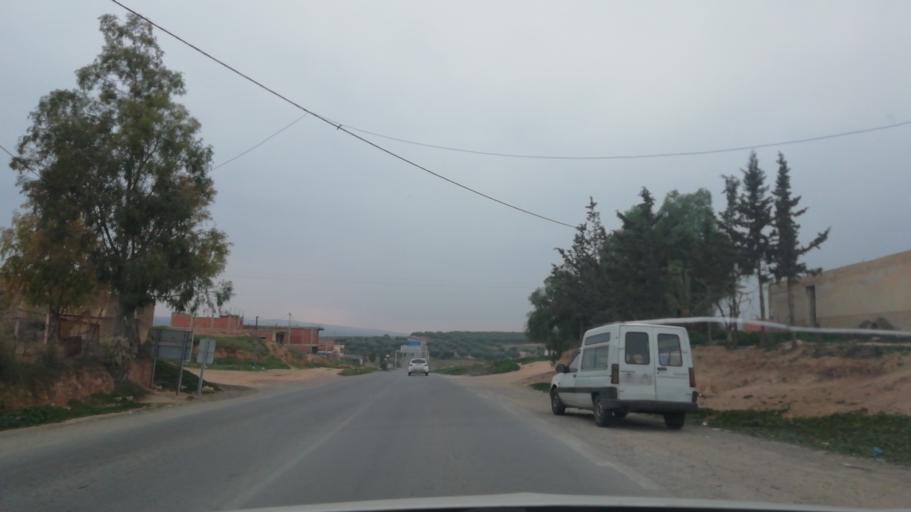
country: DZ
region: Mascara
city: Bou Hanifia el Hamamat
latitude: 35.2836
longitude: -0.1472
